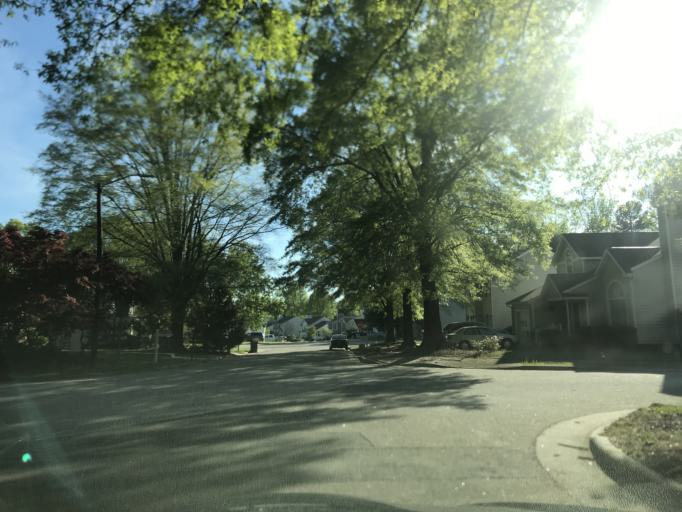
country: US
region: North Carolina
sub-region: Wake County
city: Knightdale
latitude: 35.8538
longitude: -78.5655
